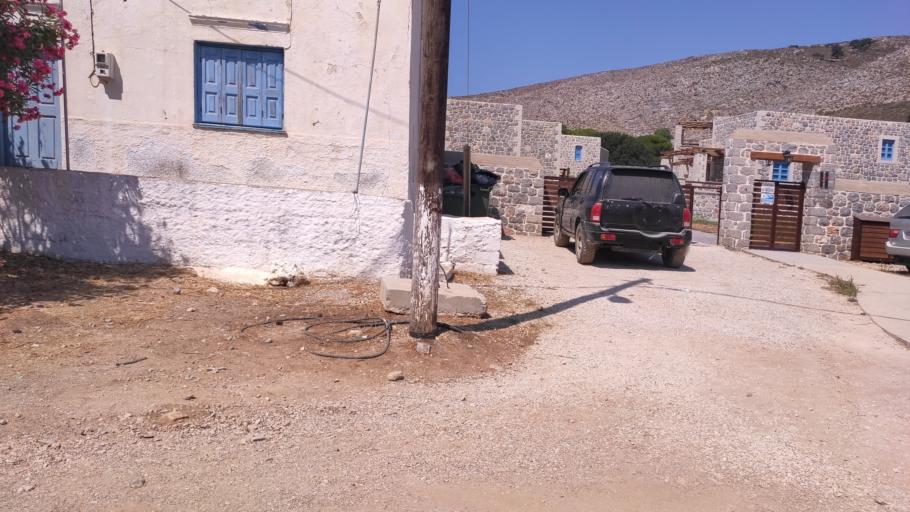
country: GR
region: South Aegean
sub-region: Nomos Dodekanisou
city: Pylion
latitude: 36.9336
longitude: 27.1345
